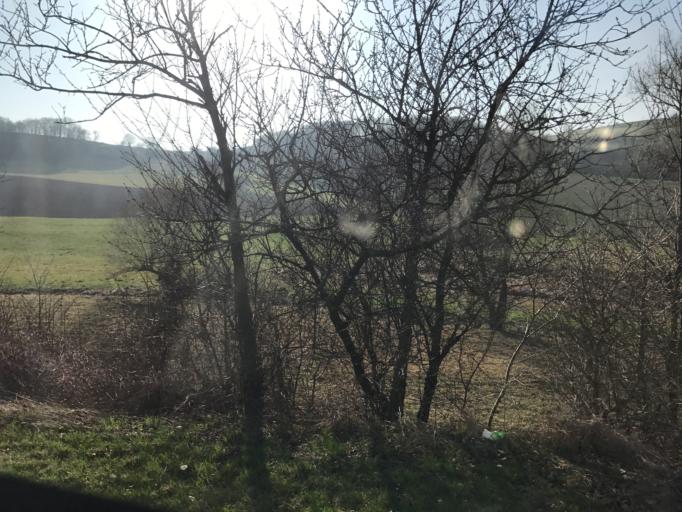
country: DE
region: Rheinland-Pfalz
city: Unkenbach
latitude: 49.7129
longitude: 7.7417
